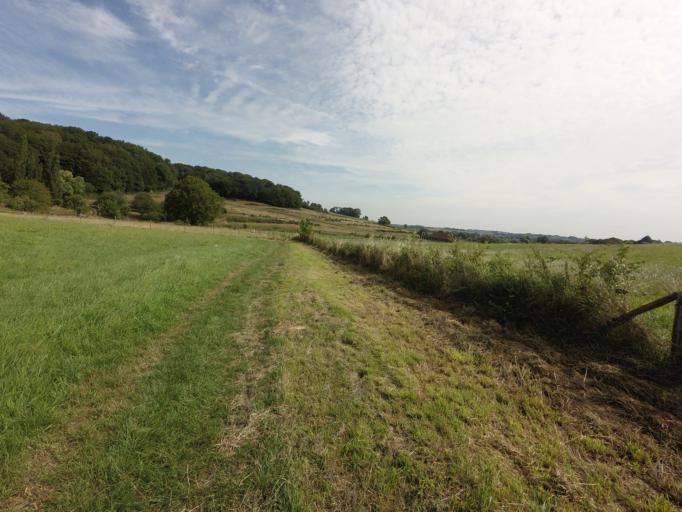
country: BE
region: Wallonia
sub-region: Province de Liege
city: Plombieres
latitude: 50.7871
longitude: 5.9042
